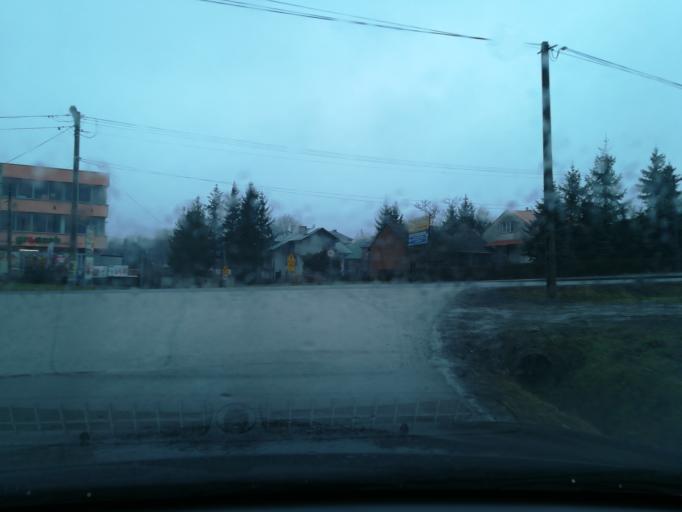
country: PL
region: Subcarpathian Voivodeship
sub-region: Powiat lancucki
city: Kosina
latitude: 50.0713
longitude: 22.3296
